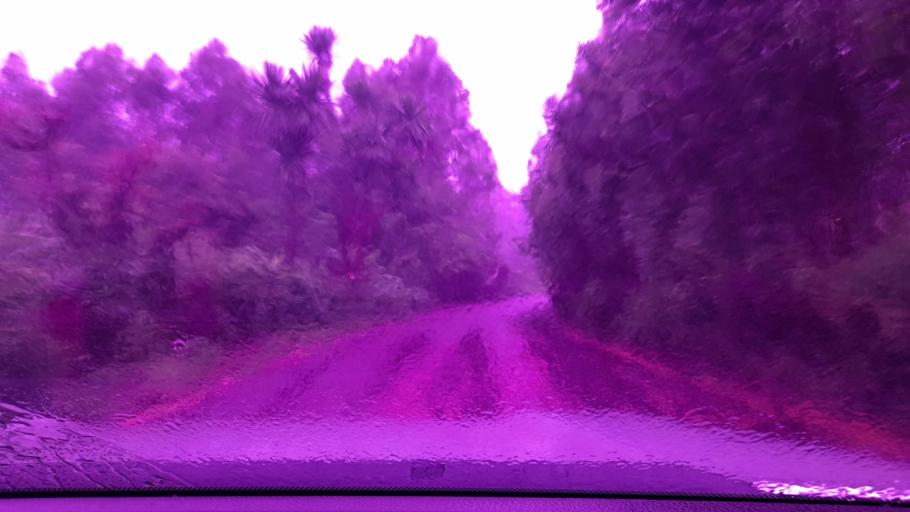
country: ET
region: Oromiya
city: Metu
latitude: 8.3600
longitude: 35.5932
